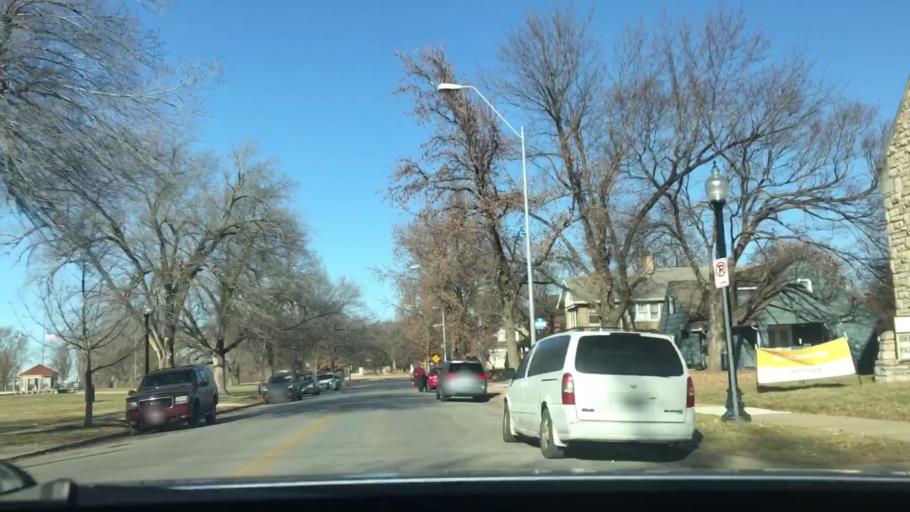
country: US
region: Missouri
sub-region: Clay County
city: North Kansas City
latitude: 39.1116
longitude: -94.5443
